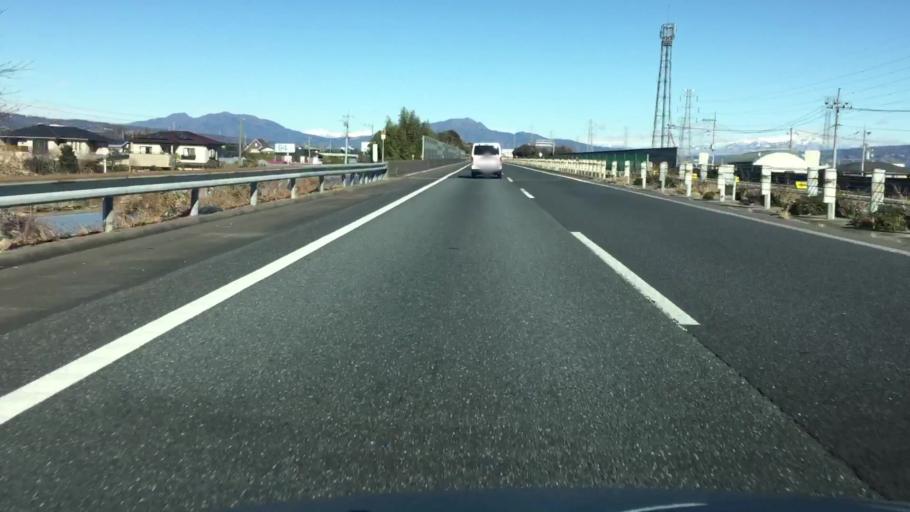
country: JP
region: Gunma
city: Kanekomachi
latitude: 36.3937
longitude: 139.0253
